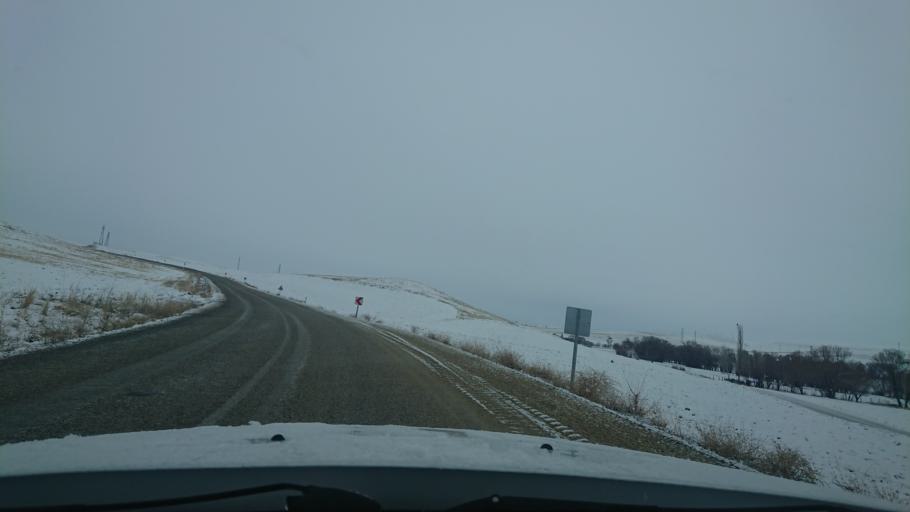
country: TR
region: Aksaray
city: Agacoren
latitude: 38.7616
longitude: 33.8706
